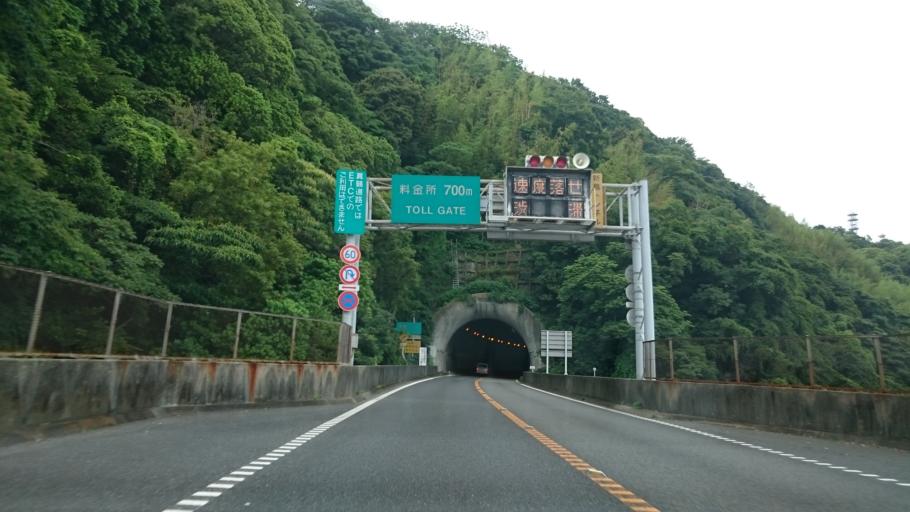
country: JP
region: Kanagawa
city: Yugawara
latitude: 35.1644
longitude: 139.1418
